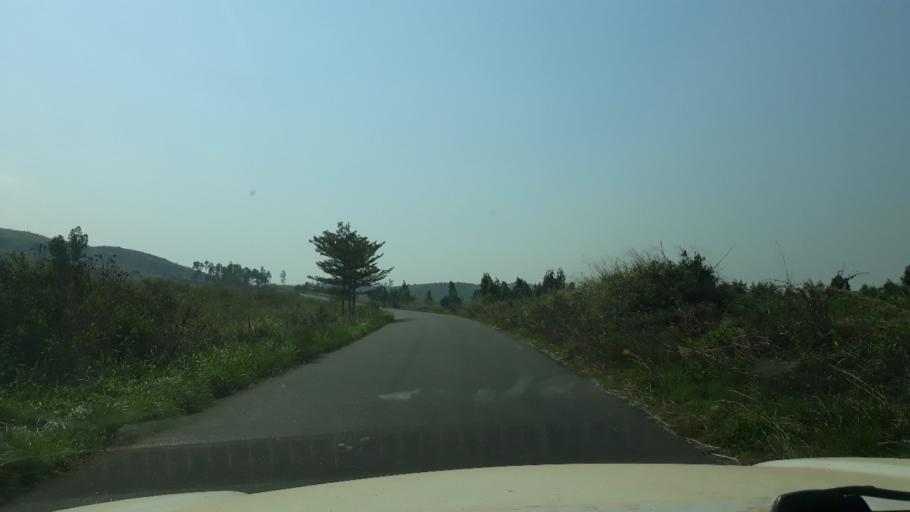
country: CD
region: South Kivu
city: Uvira
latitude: -3.2079
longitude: 29.1637
